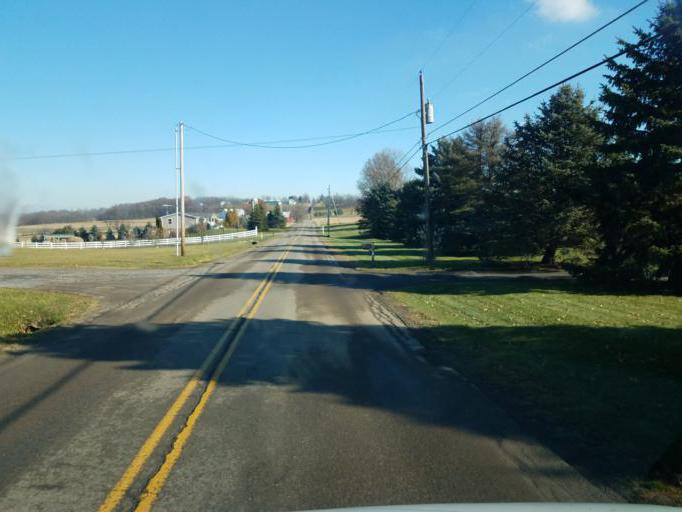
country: US
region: Ohio
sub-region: Stark County
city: Brewster
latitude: 40.6952
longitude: -81.6916
